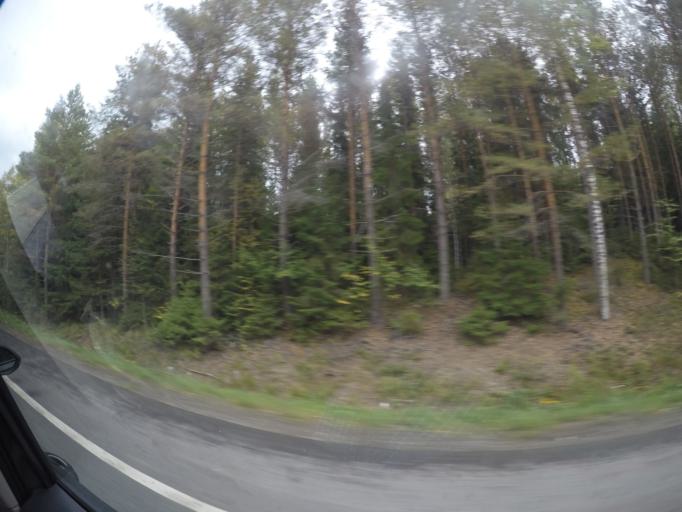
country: FI
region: Haeme
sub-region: Haemeenlinna
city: Parola
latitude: 61.1547
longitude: 24.4114
